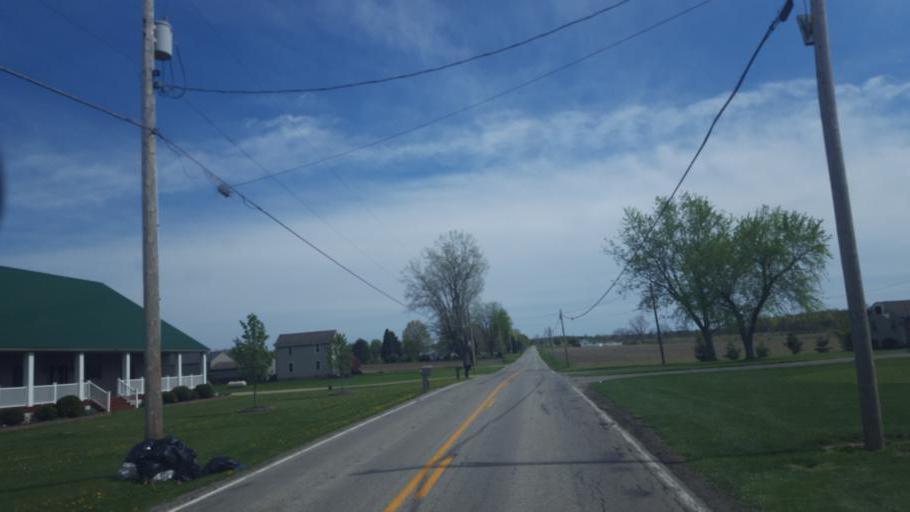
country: US
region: Ohio
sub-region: Richland County
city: Shelby
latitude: 40.8777
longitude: -82.6200
